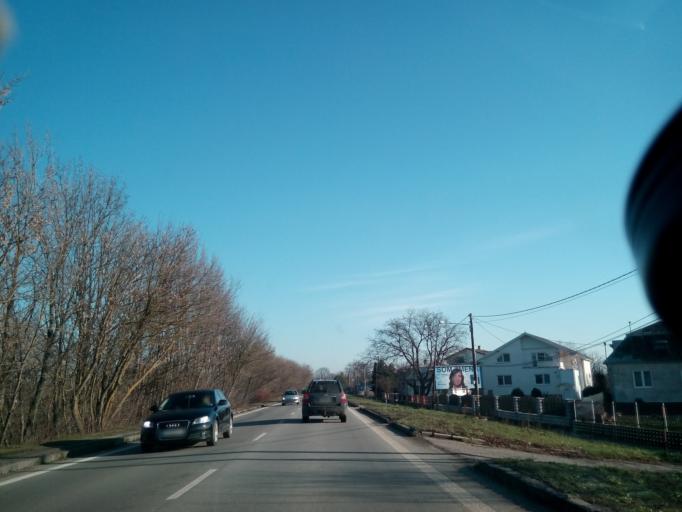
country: SK
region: Kosicky
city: Michalovce
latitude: 48.7300
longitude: 21.8697
